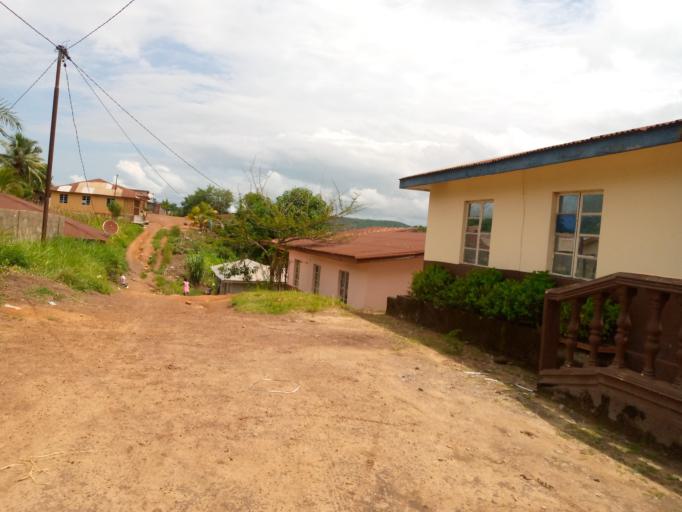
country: SL
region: Northern Province
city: Magburaka
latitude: 8.7256
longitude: -11.9379
